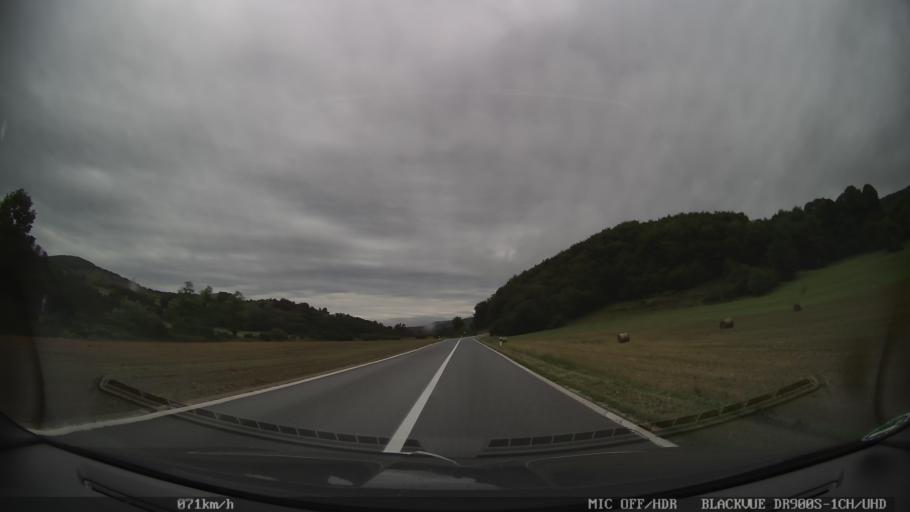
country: HR
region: Licko-Senjska
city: Brinje
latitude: 44.9320
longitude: 15.1328
